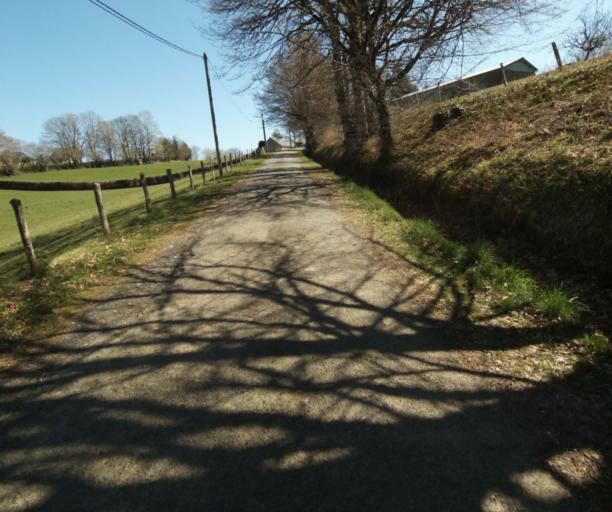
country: FR
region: Limousin
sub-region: Departement de la Correze
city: Saint-Clement
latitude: 45.3257
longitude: 1.7079
